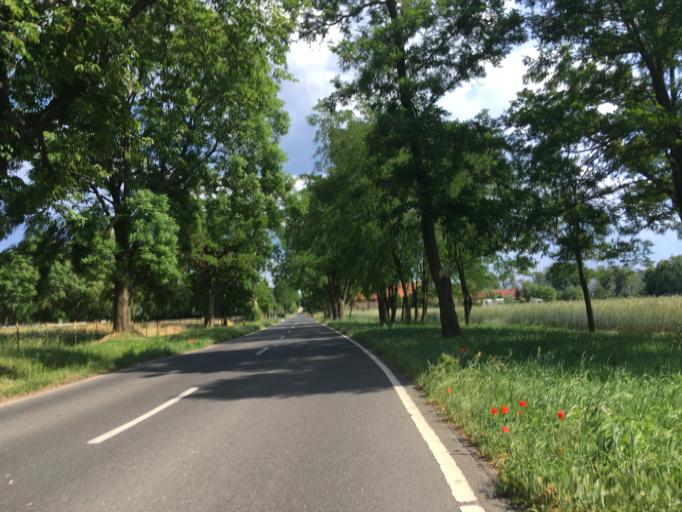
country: DE
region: Brandenburg
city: Steinhofel
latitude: 52.4259
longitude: 14.1083
